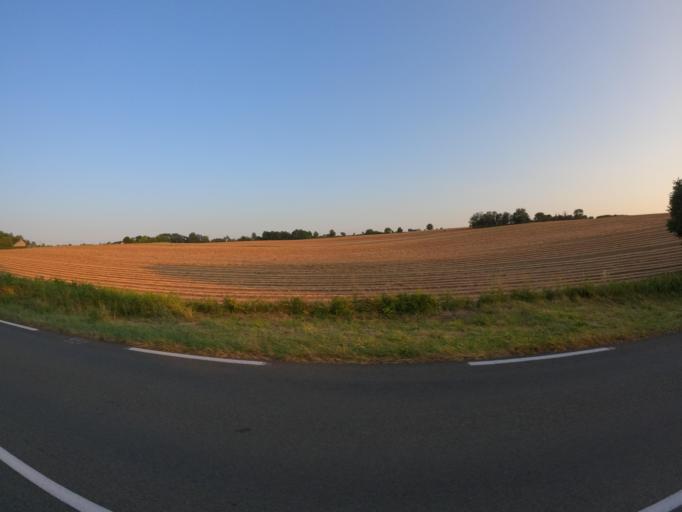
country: FR
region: Pays de la Loire
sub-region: Departement de la Mayenne
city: Meslay-du-Maine
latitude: 47.8717
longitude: -0.4918
